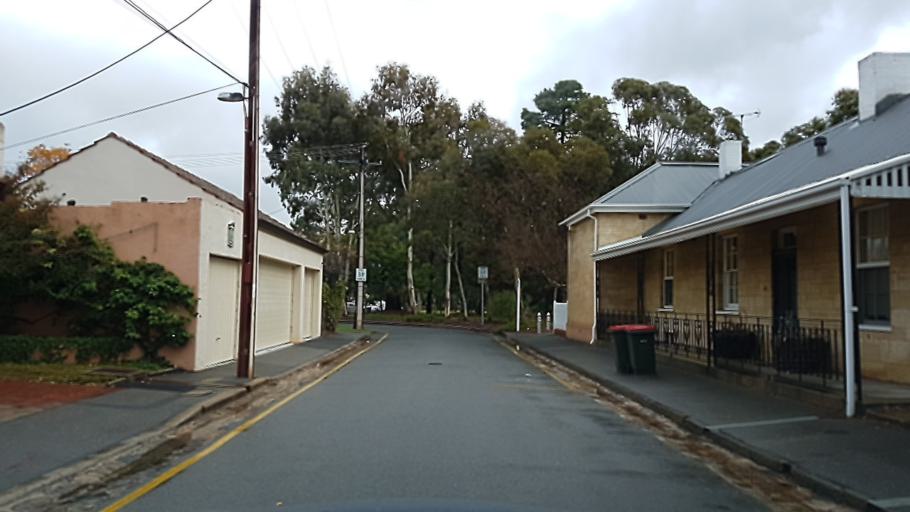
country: AU
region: South Australia
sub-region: Adelaide
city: North Adelaide
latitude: -34.9039
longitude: 138.6076
